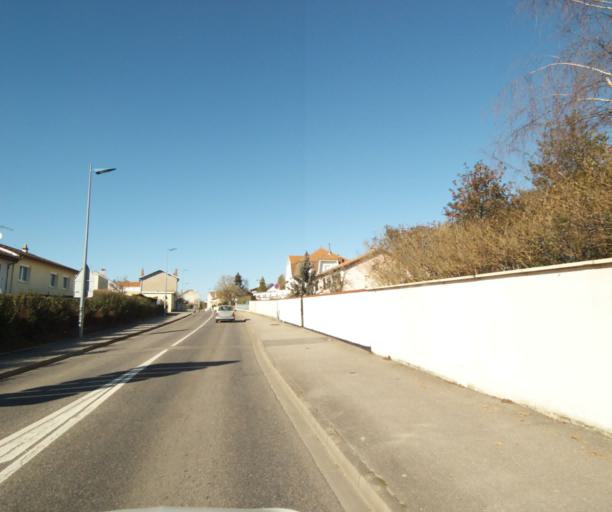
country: FR
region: Lorraine
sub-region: Departement de Meurthe-et-Moselle
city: Tomblaine
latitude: 48.6823
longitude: 6.2158
